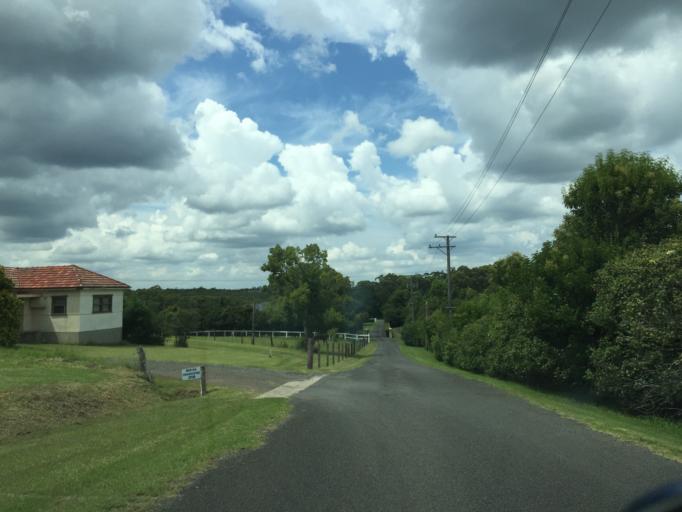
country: AU
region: New South Wales
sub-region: Hornsby Shire
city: Galston
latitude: -33.6569
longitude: 151.0528
